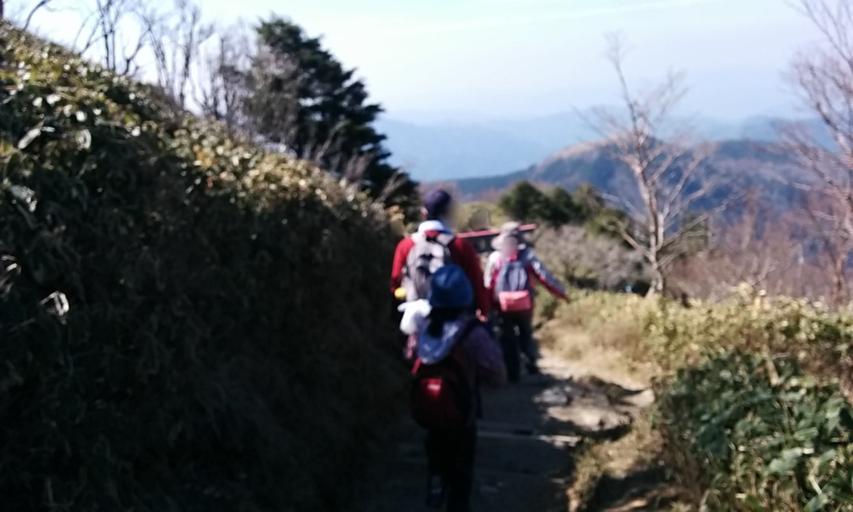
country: JP
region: Tokushima
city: Wakimachi
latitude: 33.8554
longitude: 134.0959
